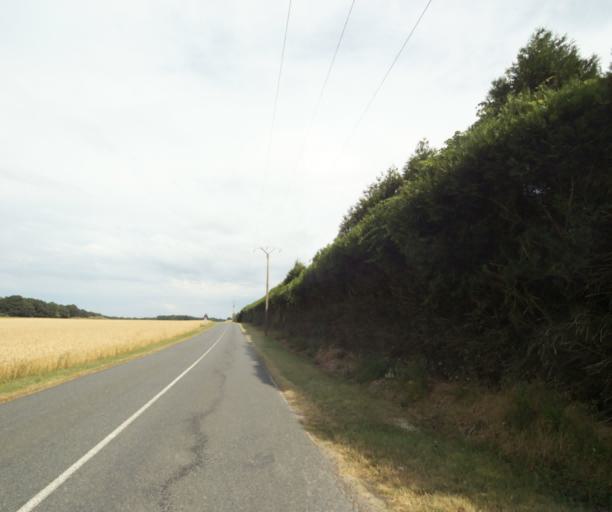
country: FR
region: Ile-de-France
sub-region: Departement de Seine-et-Marne
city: Acheres-la-Foret
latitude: 48.3505
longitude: 2.5774
